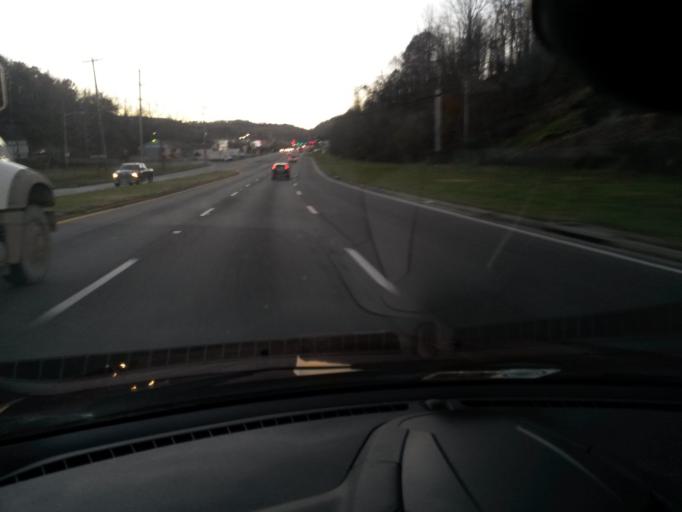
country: US
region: Virginia
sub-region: Roanoke County
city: Narrows
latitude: 37.2297
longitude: -79.9715
